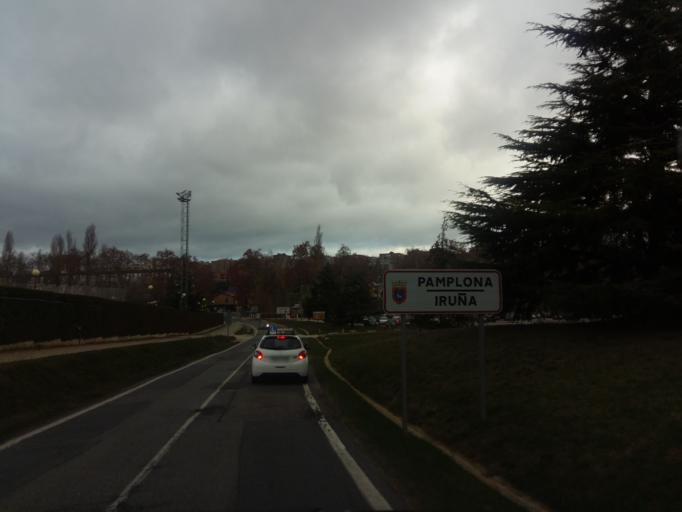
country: ES
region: Navarre
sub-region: Provincia de Navarra
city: Iturrama
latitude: 42.7975
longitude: -1.6531
